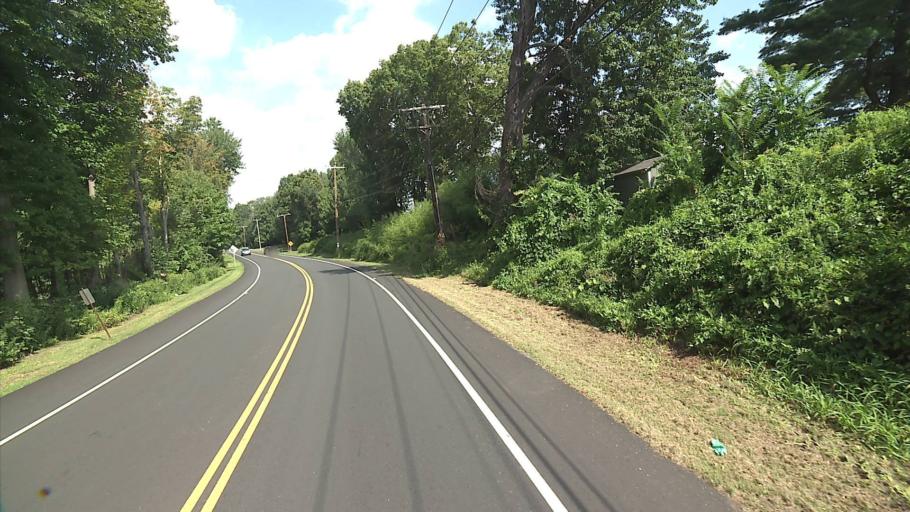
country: US
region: Connecticut
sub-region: Hartford County
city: West Hartford
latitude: 41.8100
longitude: -72.7576
